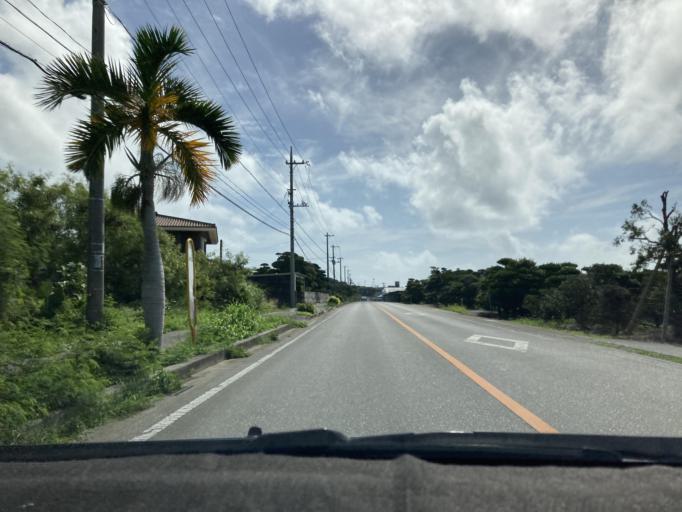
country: JP
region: Okinawa
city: Itoman
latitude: 26.1006
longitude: 127.6738
